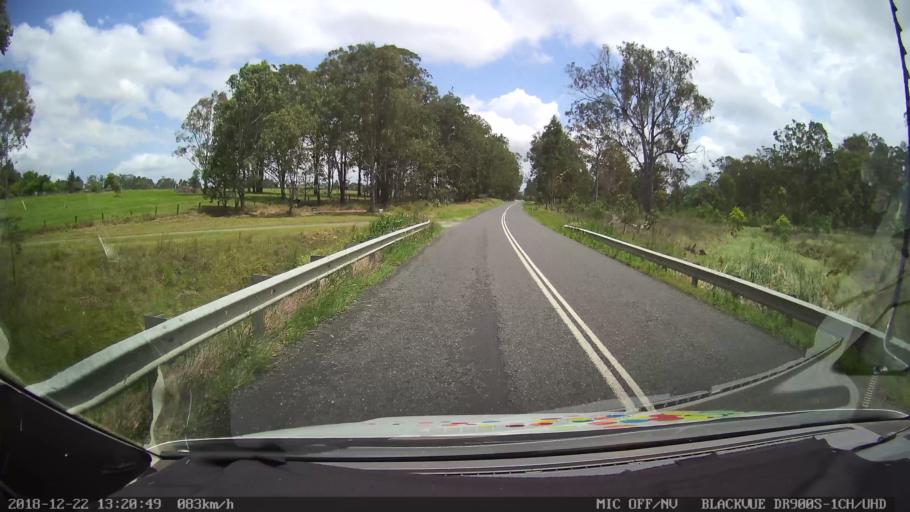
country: AU
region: New South Wales
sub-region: Clarence Valley
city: South Grafton
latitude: -29.7707
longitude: 152.9258
